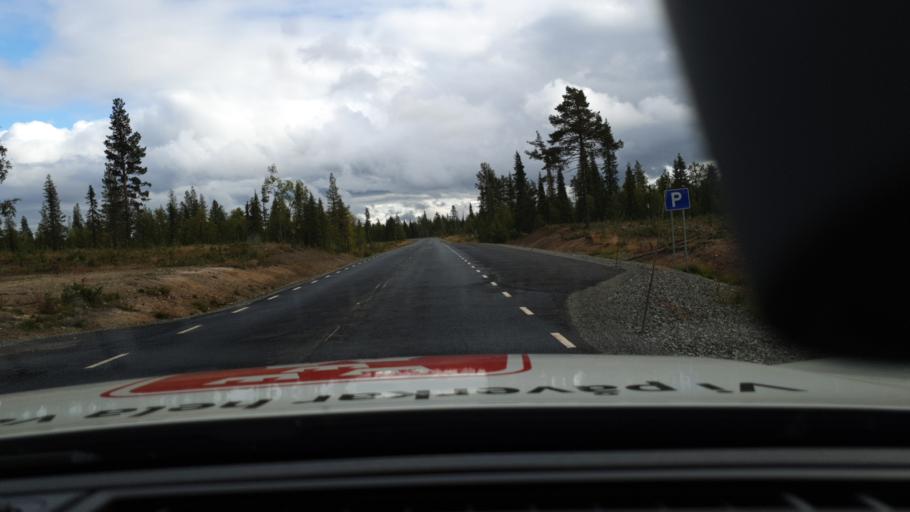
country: SE
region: Norrbotten
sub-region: Gallivare Kommun
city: Gaellivare
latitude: 66.8521
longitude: 21.0942
